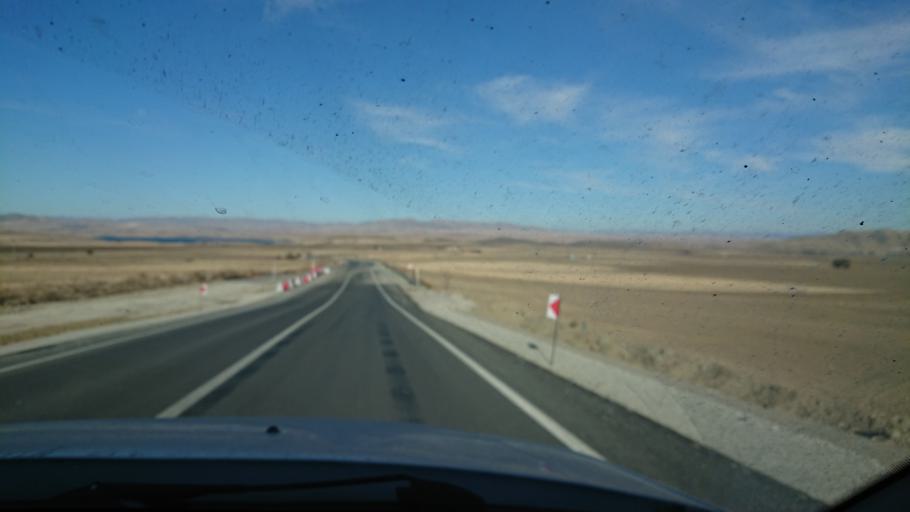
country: TR
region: Aksaray
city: Sariyahsi
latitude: 38.9997
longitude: 33.8543
